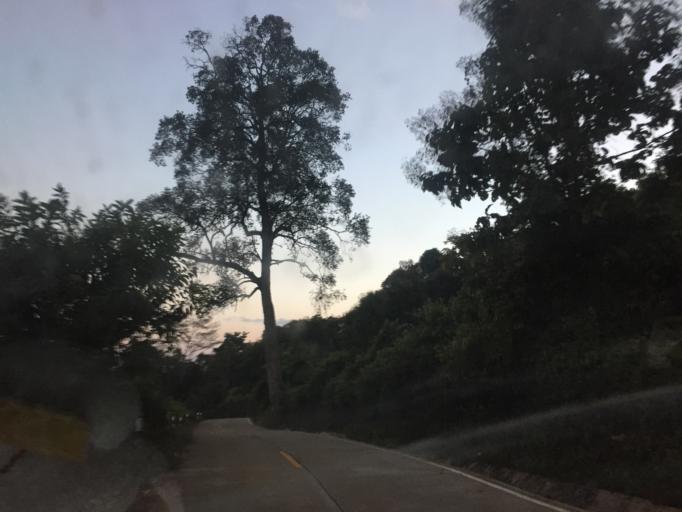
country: TH
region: Chiang Mai
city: Samoeng
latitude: 18.9915
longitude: 98.7183
